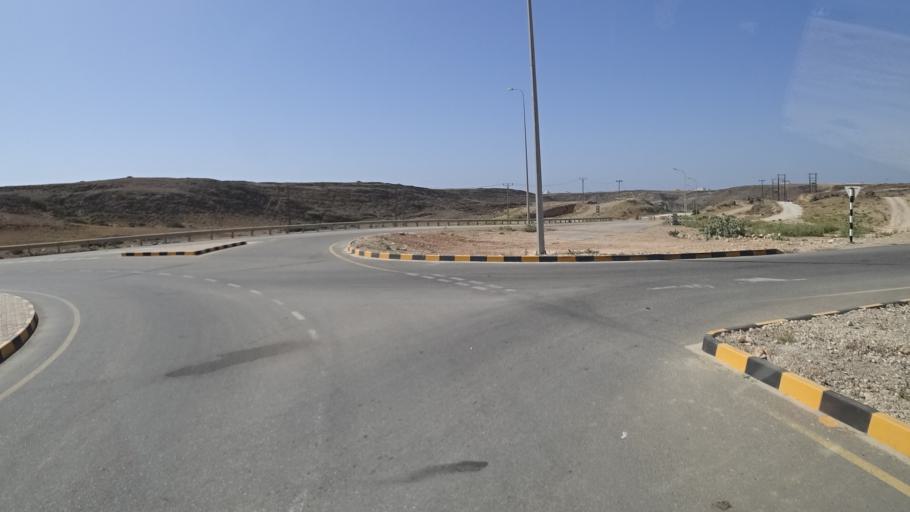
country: OM
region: Zufar
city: Salalah
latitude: 17.0587
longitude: 54.4318
